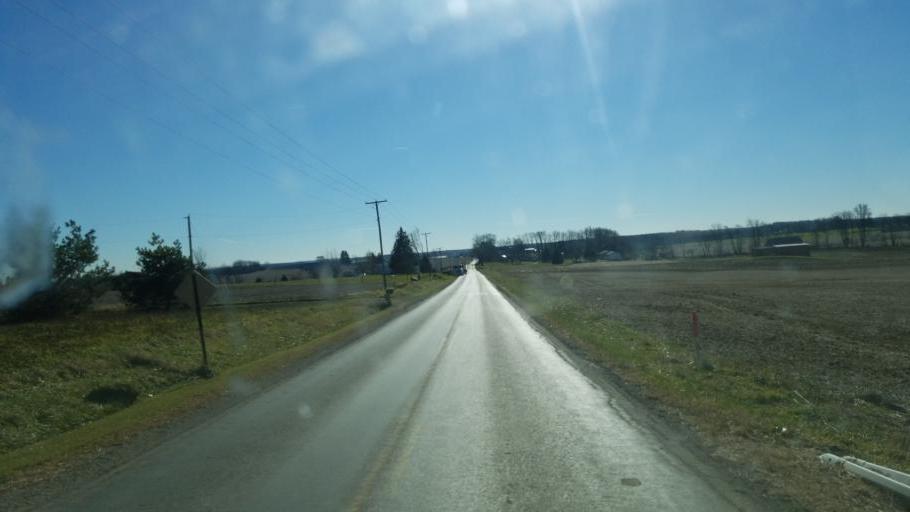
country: US
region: Ohio
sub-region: Huron County
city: Plymouth
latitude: 40.9455
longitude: -82.5833
